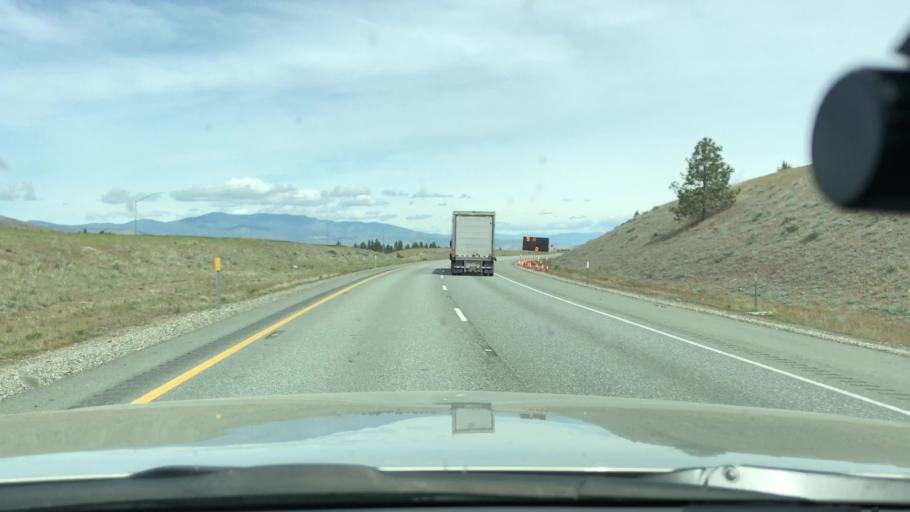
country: US
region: California
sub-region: Siskiyou County
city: Weed
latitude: 41.4514
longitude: -122.4419
